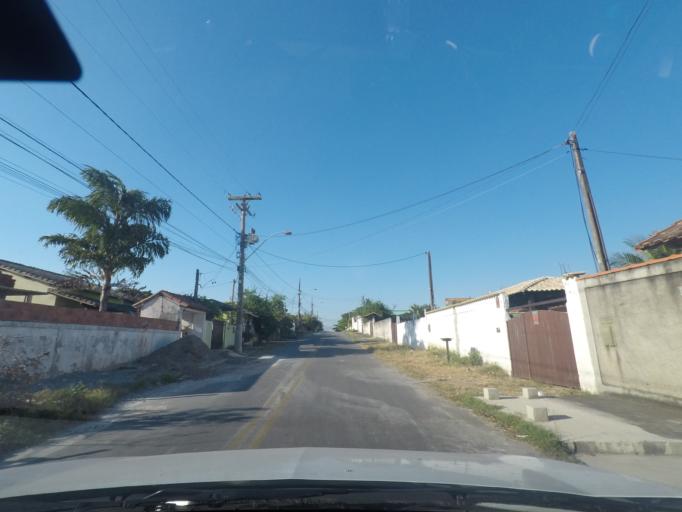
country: BR
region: Rio de Janeiro
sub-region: Marica
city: Marica
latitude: -22.9687
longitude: -42.9388
